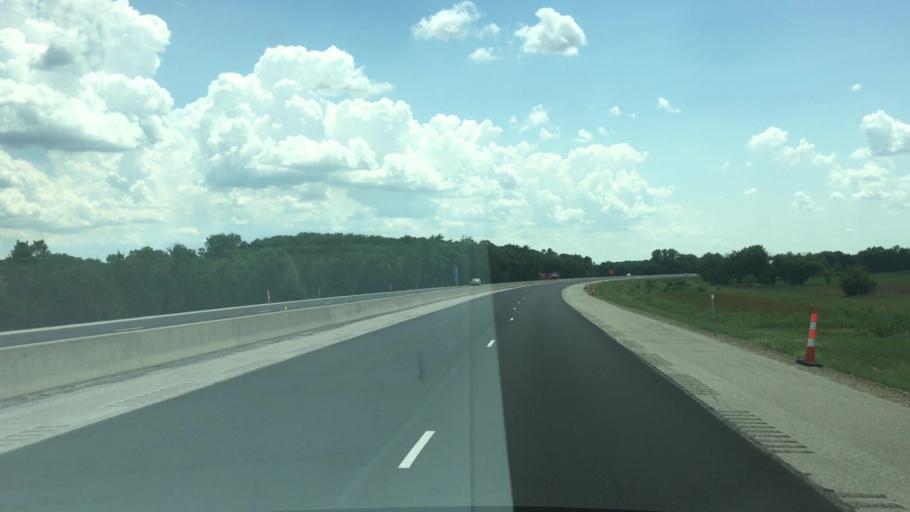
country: US
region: Kansas
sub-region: Lyon County
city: Emporia
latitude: 38.5033
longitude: -96.1517
